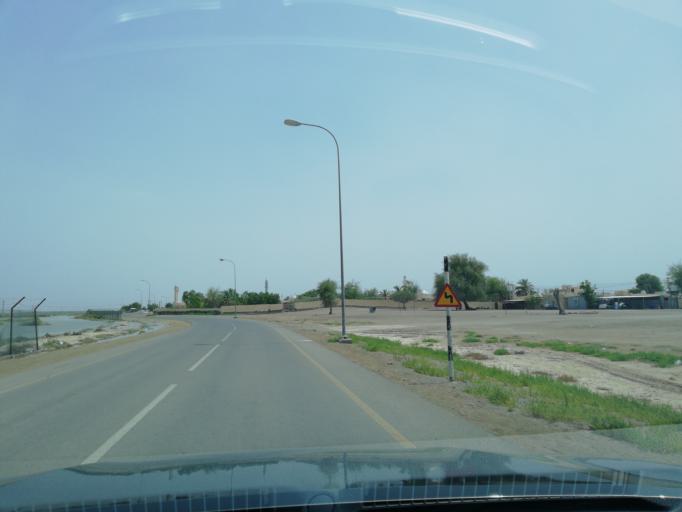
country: OM
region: Al Batinah
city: Shinas
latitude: 24.7482
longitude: 56.4676
